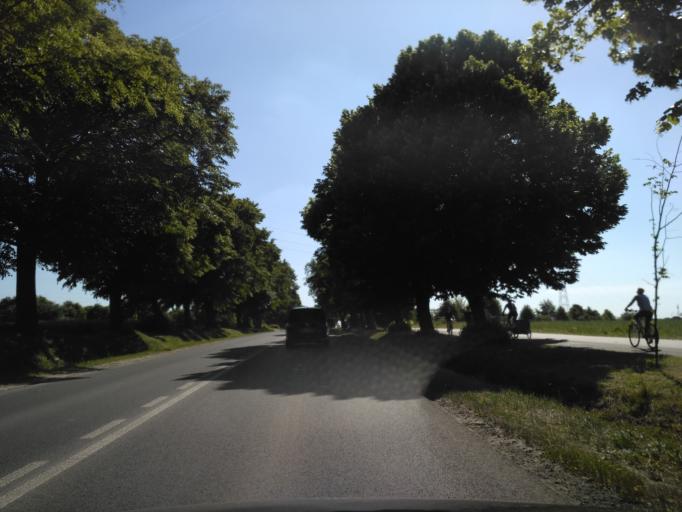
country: PL
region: Lublin Voivodeship
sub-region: Powiat lubelski
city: Lublin
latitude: 51.1968
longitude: 22.5499
